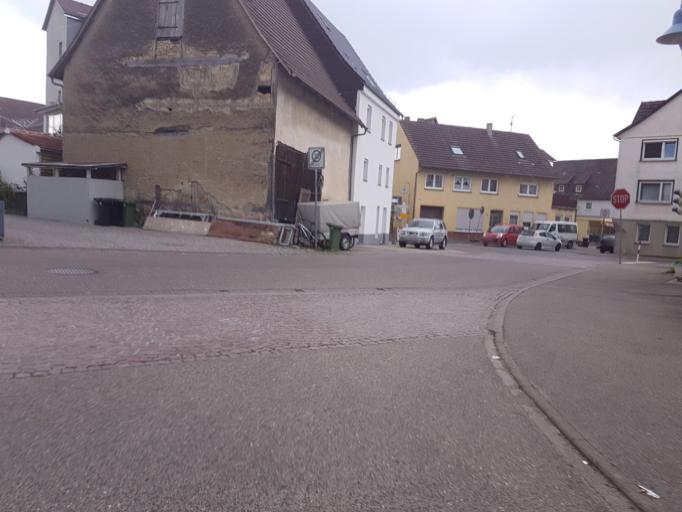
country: DE
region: Baden-Wuerttemberg
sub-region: Regierungsbezirk Stuttgart
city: Bondorf
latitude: 48.4967
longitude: 8.8080
